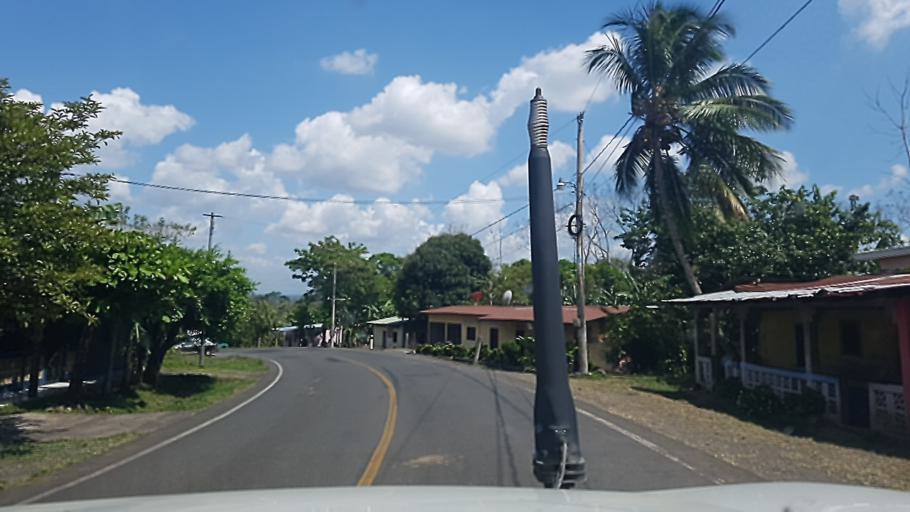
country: NI
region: Atlantico Sur
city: Muelle de los Bueyes
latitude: 11.9144
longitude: -84.6445
